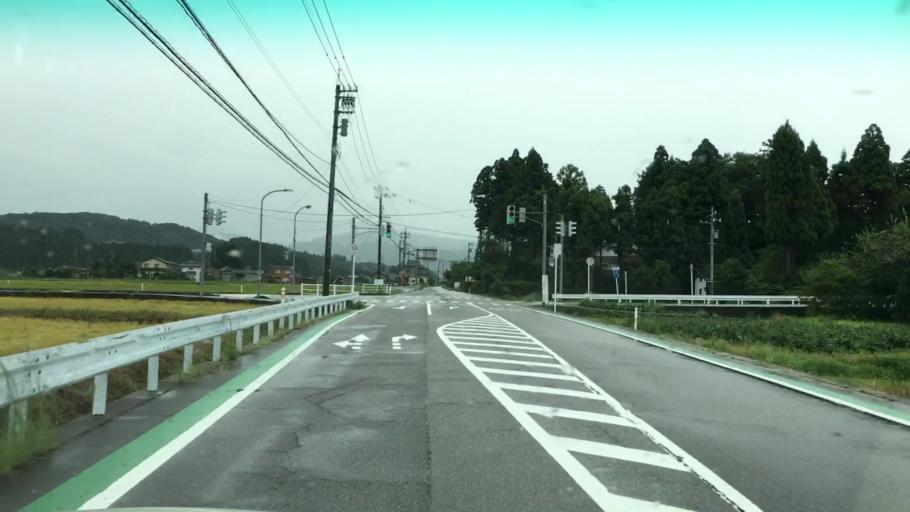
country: JP
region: Toyama
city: Kamiichi
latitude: 36.6261
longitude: 137.3229
